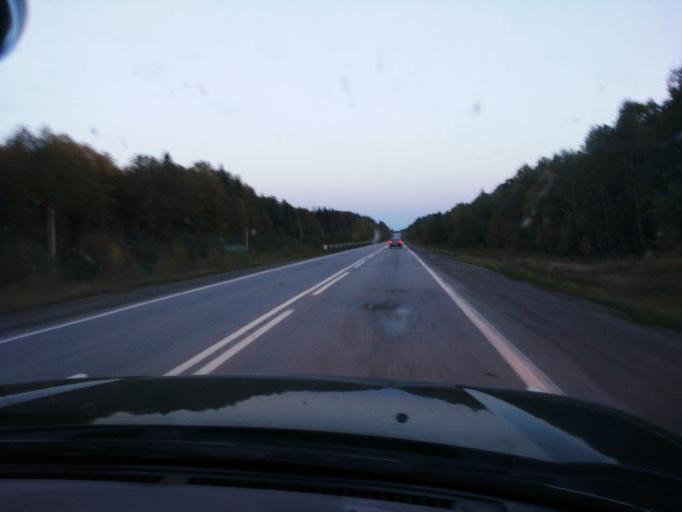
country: RU
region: Perm
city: Verkhnechusovskiye Gorodki
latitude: 58.2748
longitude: 56.9392
